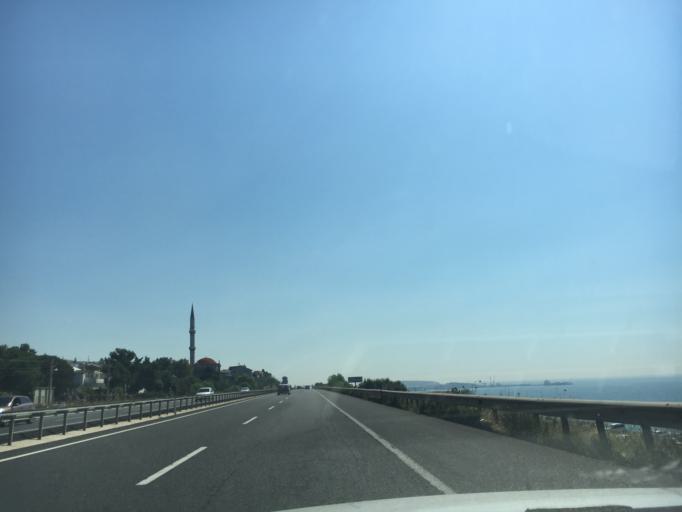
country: TR
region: Tekirdag
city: Marmara Ereglisi
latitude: 40.9691
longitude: 27.8990
